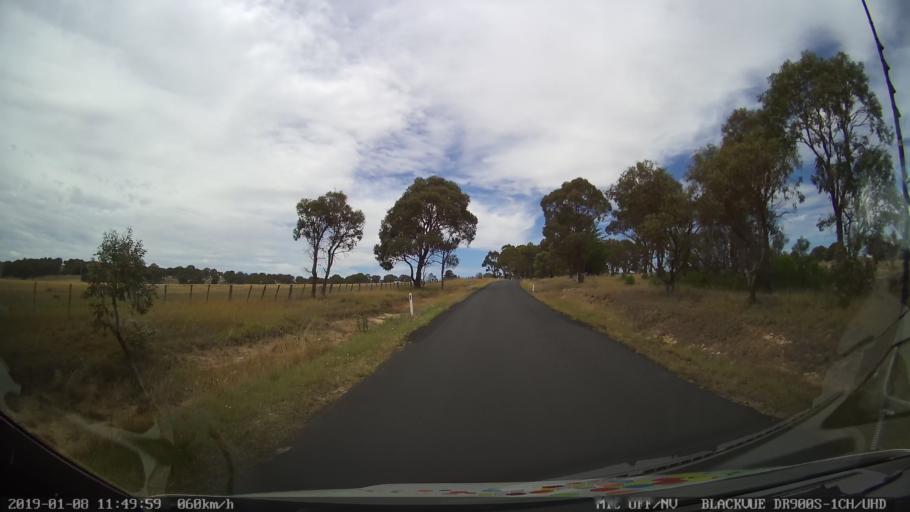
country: AU
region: New South Wales
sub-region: Armidale Dumaresq
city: Armidale
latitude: -30.3786
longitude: 151.5585
